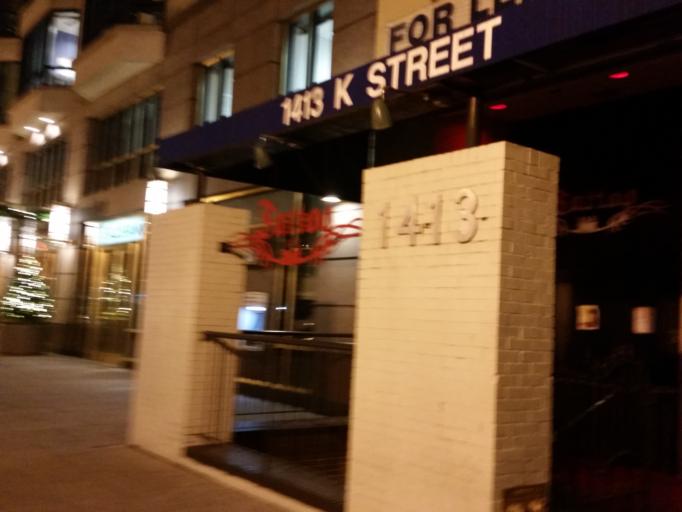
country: US
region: Washington, D.C.
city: Washington, D.C.
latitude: 38.9028
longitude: -77.0323
